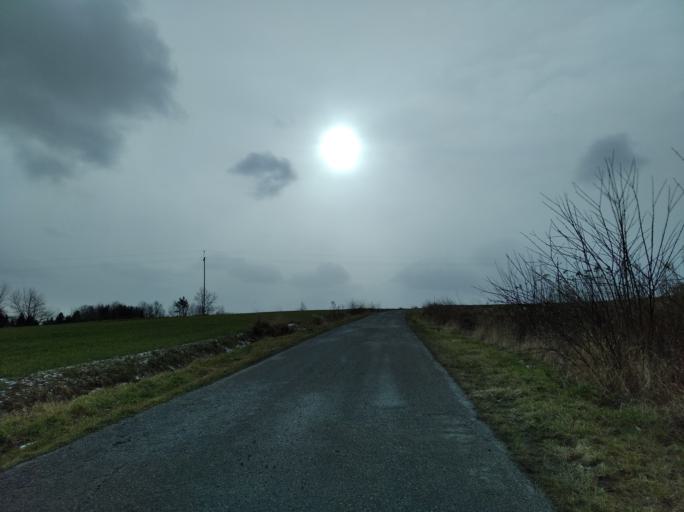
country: PL
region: Subcarpathian Voivodeship
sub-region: Powiat strzyzowski
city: Strzyzow
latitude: 49.8973
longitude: 21.7373
